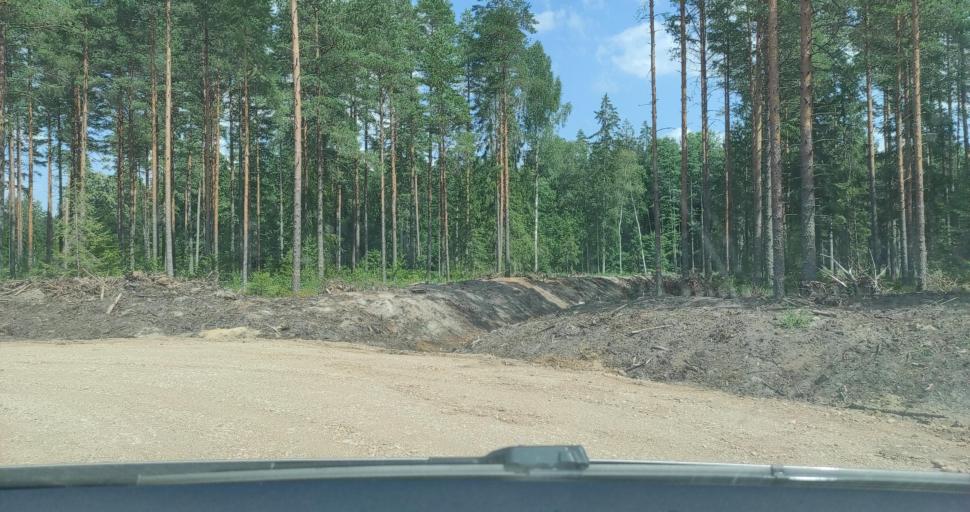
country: LV
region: Kuldigas Rajons
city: Kuldiga
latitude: 57.0526
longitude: 22.1909
